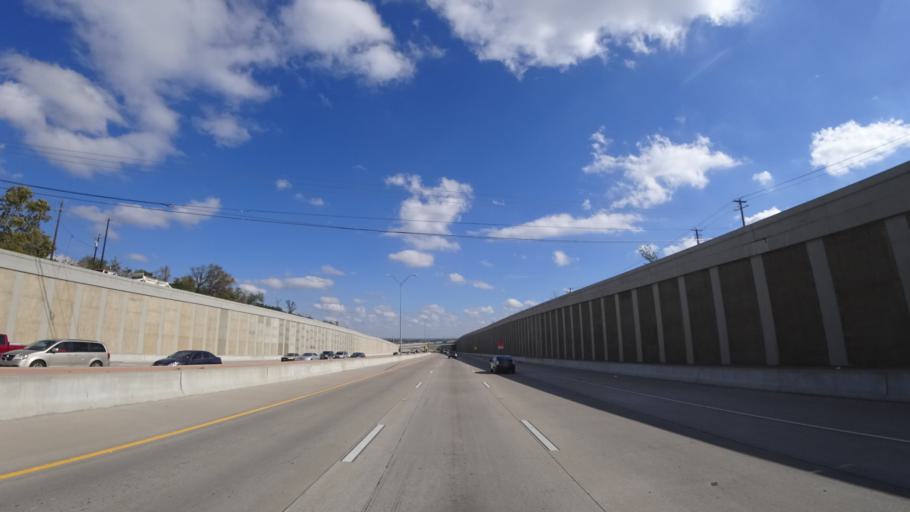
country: US
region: Texas
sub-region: Travis County
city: Austin
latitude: 30.2171
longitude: -97.6946
